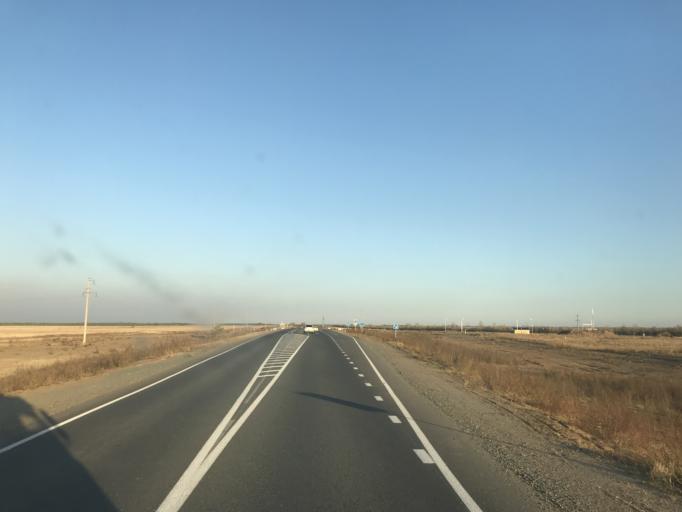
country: KZ
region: Pavlodar
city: Kurchatov
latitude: 50.9614
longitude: 79.3342
